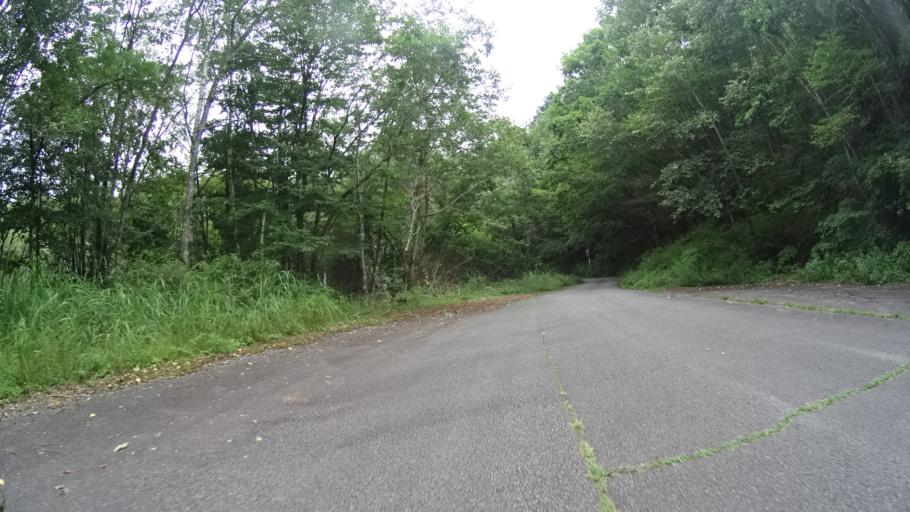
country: JP
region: Yamanashi
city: Enzan
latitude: 35.8024
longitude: 138.6326
